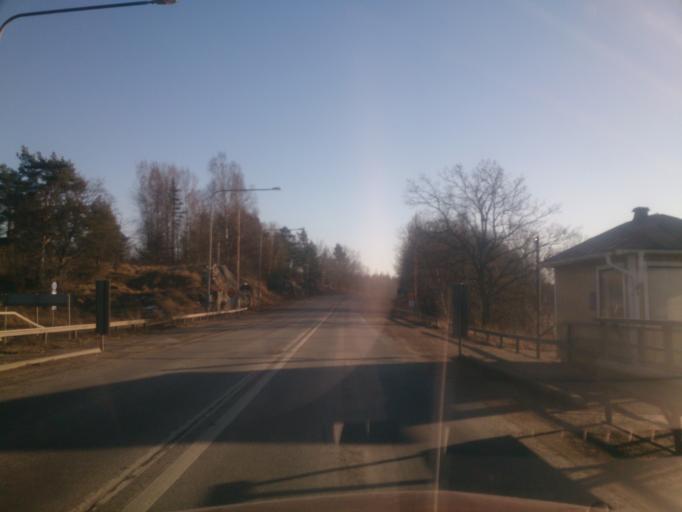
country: SE
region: OEstergoetland
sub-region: Norrkopings Kommun
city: Kimstad
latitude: 58.5087
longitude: 15.9818
